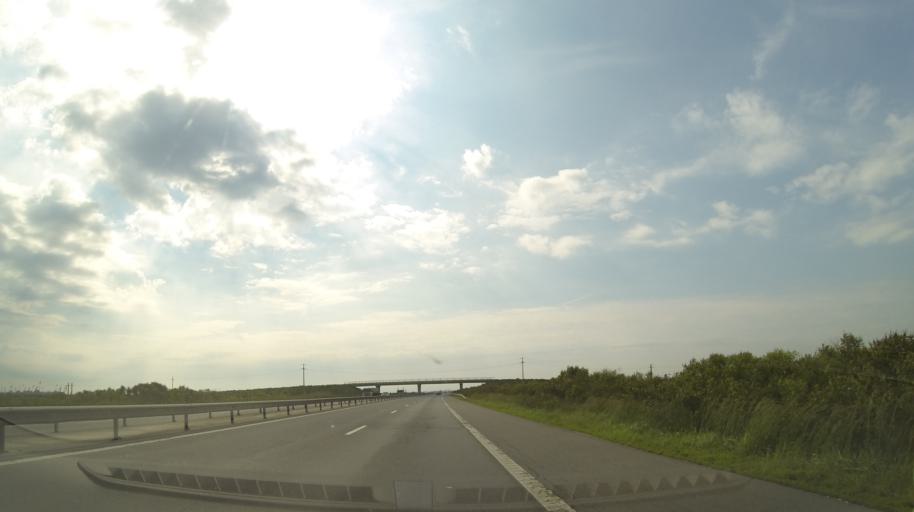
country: RO
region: Dambovita
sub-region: Comuna Corbii Mari
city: Ungureni
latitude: 44.5647
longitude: 25.4910
